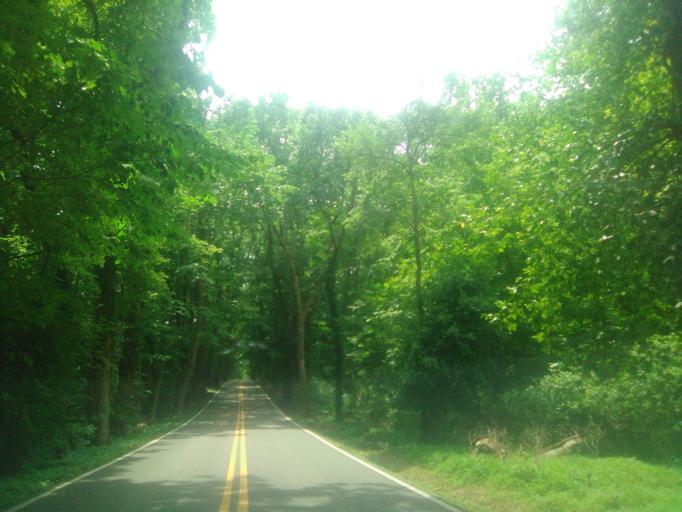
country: US
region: Tennessee
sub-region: Davidson County
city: Belle Meade
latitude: 36.0764
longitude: -86.8694
